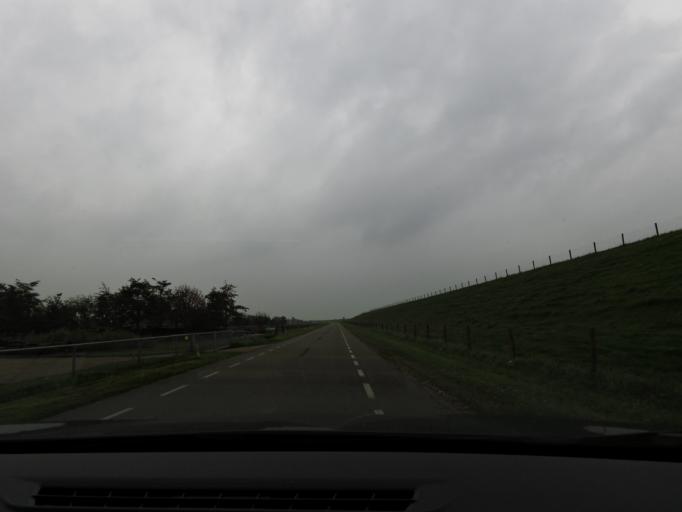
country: NL
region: South Holland
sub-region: Gemeente Hellevoetsluis
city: Hellevoetsluis
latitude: 51.8166
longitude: 4.1682
